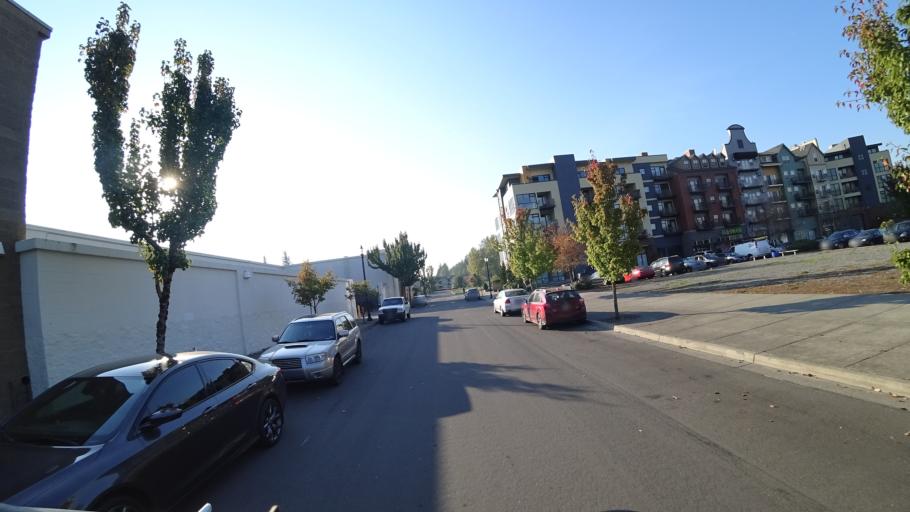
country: US
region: Oregon
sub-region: Multnomah County
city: Gresham
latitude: 45.5067
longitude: -122.4401
